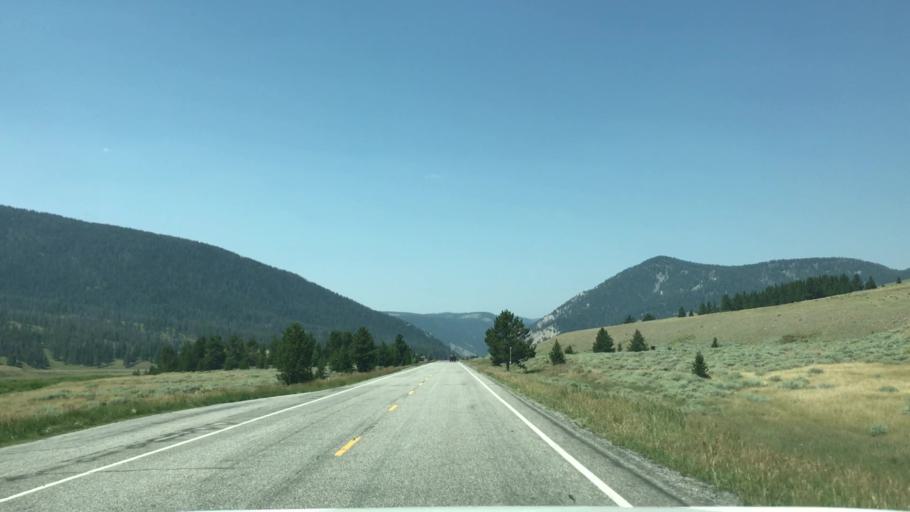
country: US
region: Montana
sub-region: Gallatin County
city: Big Sky
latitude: 45.0466
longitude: -111.1360
